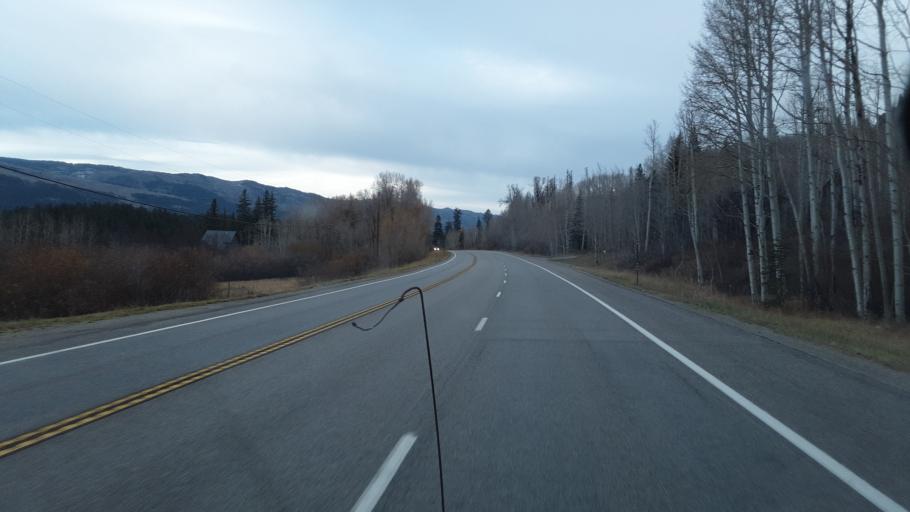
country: US
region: Colorado
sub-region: La Plata County
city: Durango
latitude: 37.5426
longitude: -107.8231
